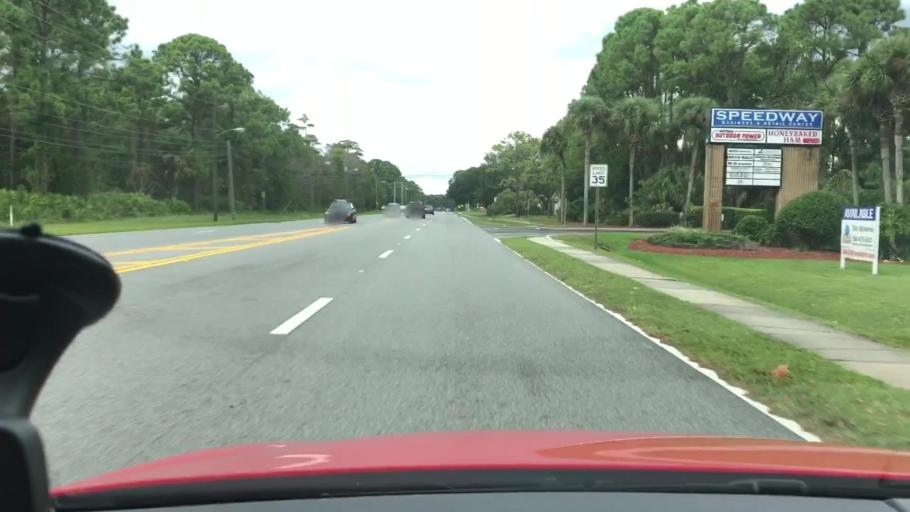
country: US
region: Florida
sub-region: Volusia County
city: Daytona Beach
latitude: 29.1979
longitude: -81.0693
